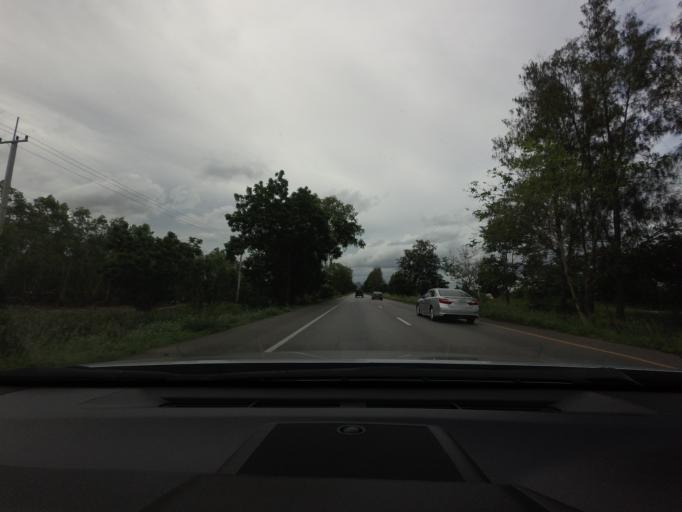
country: TH
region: Phetchaburi
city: Cha-am
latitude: 12.7374
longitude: 99.9285
